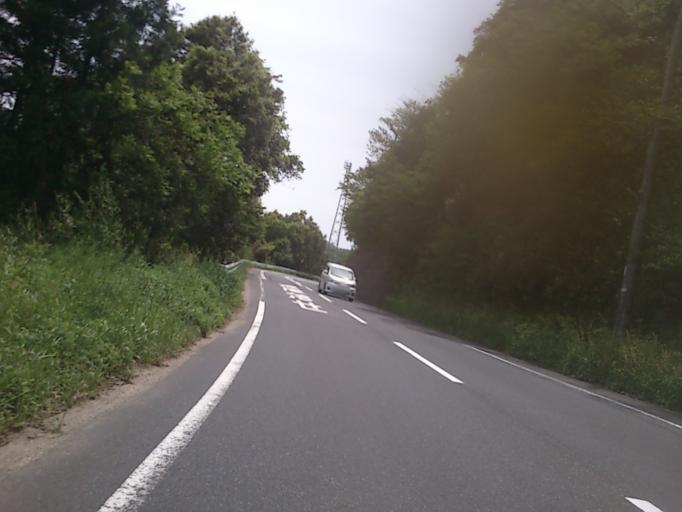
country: JP
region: Kyoto
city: Miyazu
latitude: 35.6481
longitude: 135.0848
